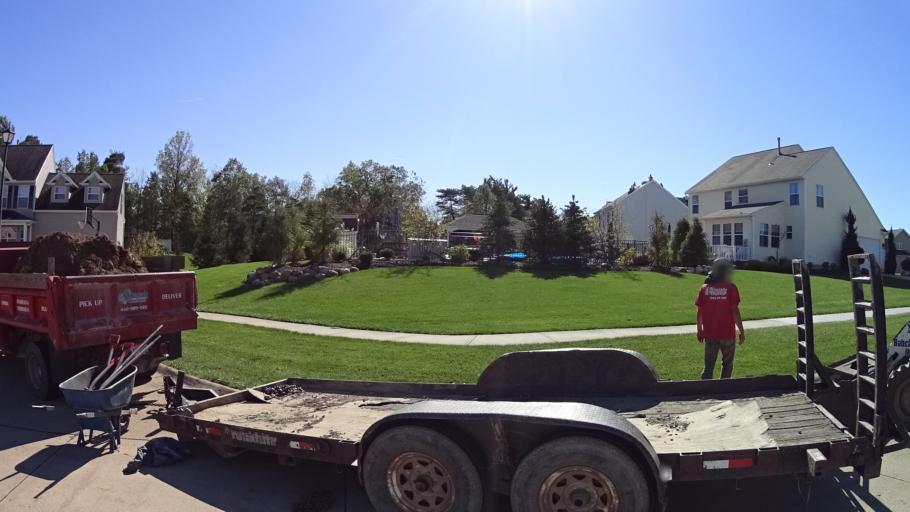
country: US
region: Ohio
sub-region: Lorain County
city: Amherst
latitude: 41.3847
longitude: -82.2406
